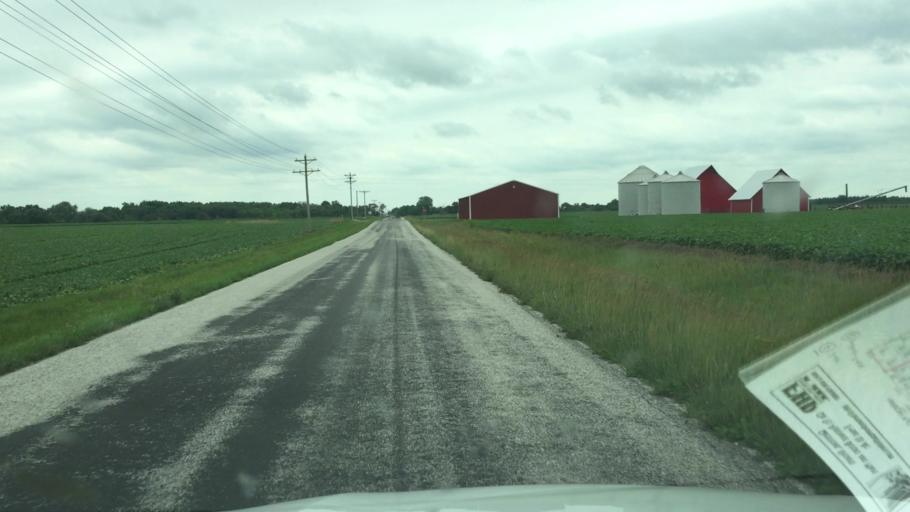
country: US
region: Illinois
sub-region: Hancock County
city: Carthage
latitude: 40.2920
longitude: -91.0833
